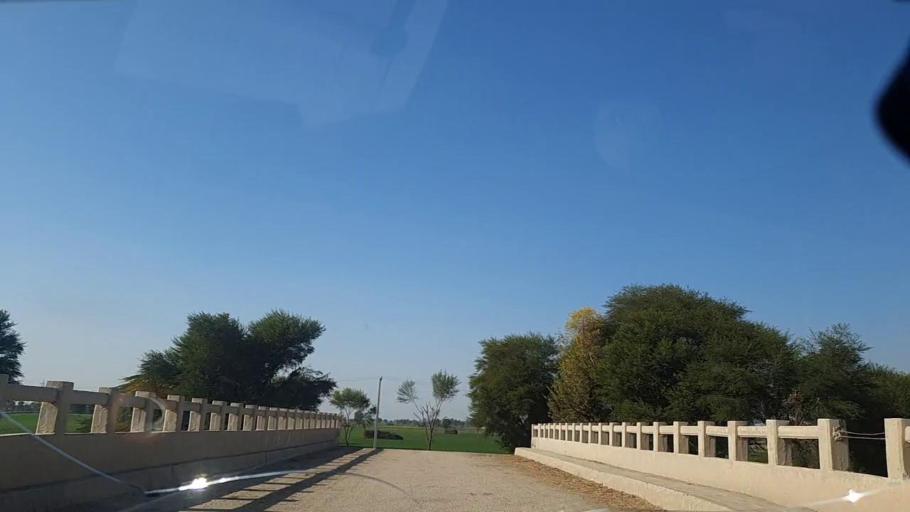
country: PK
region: Sindh
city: Khanpur
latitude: 27.7901
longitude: 69.3507
